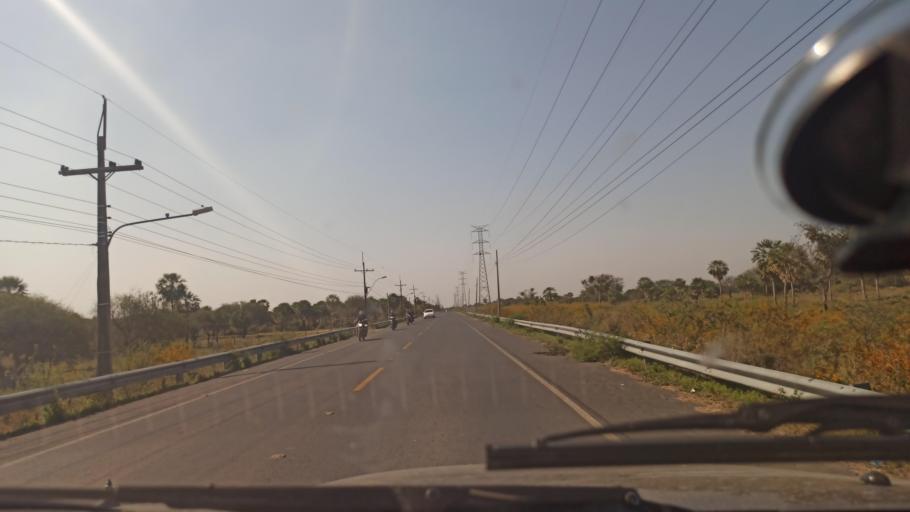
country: PY
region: Presidente Hayes
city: Nanawa
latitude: -25.2543
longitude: -57.6752
